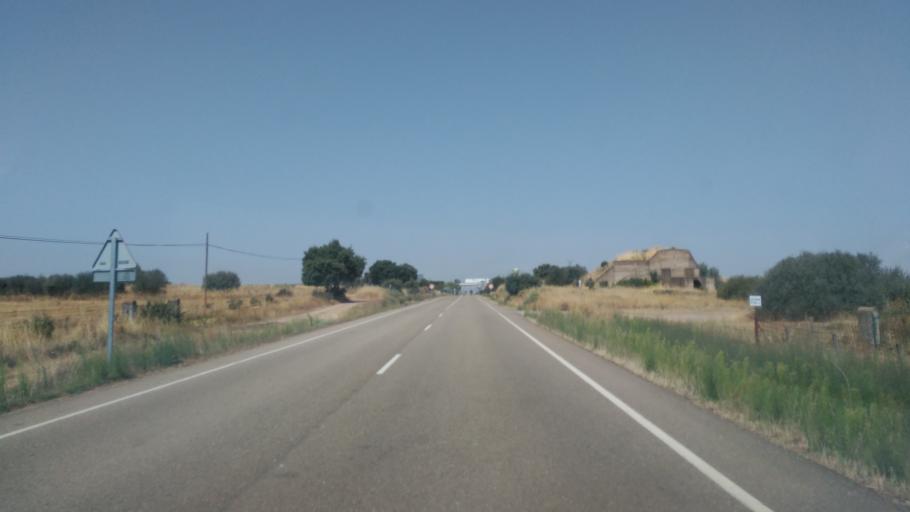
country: ES
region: Castille and Leon
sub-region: Provincia de Salamanca
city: La Fuente de San Esteban
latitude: 40.7835
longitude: -6.2361
